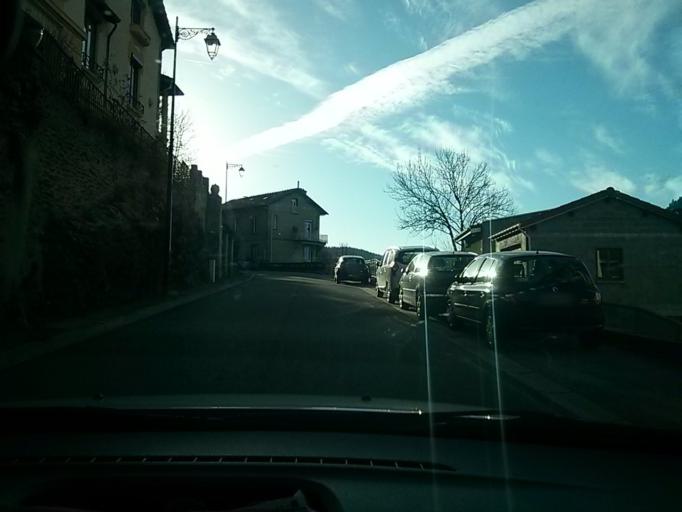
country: FR
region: Rhone-Alpes
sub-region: Departement de la Loire
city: Saint-Jean-Bonnefonds
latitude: 45.4089
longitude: 4.4468
